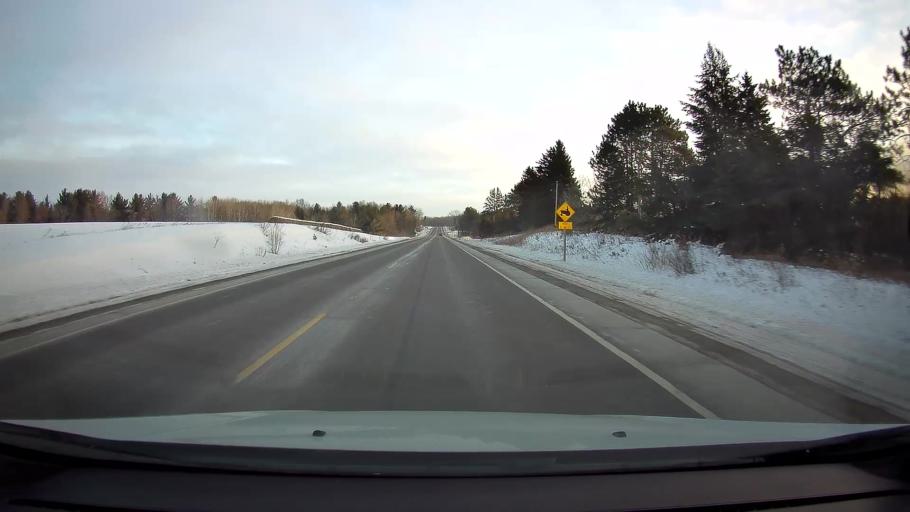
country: US
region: Wisconsin
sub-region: Polk County
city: Clear Lake
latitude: 45.2609
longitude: -92.2589
